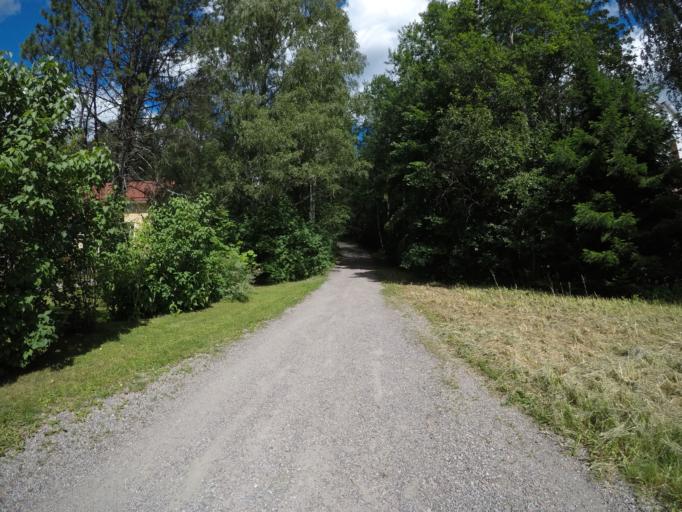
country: FI
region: Haeme
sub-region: Haemeenlinna
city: Haemeenlinna
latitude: 61.0114
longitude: 24.4394
